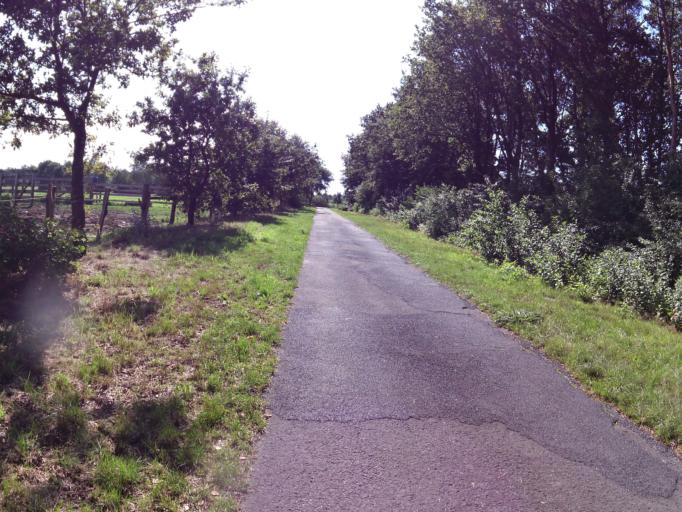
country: DE
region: Lower Saxony
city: Sandbostel
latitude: 53.3894
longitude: 9.1222
